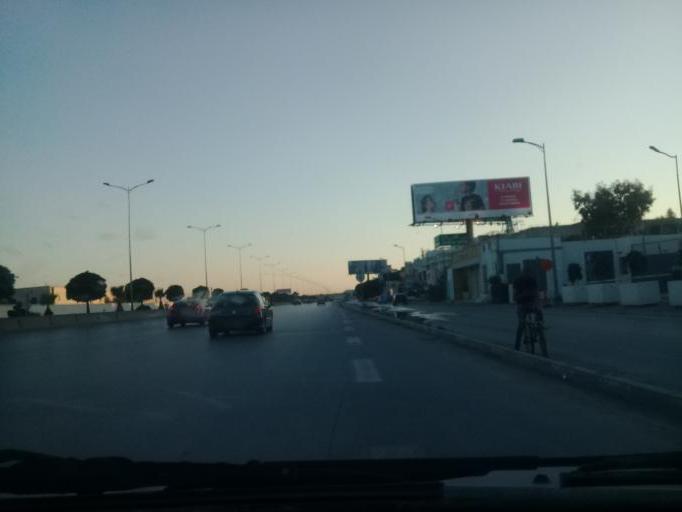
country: TN
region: Tunis
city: La Goulette
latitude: 36.8519
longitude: 10.2701
